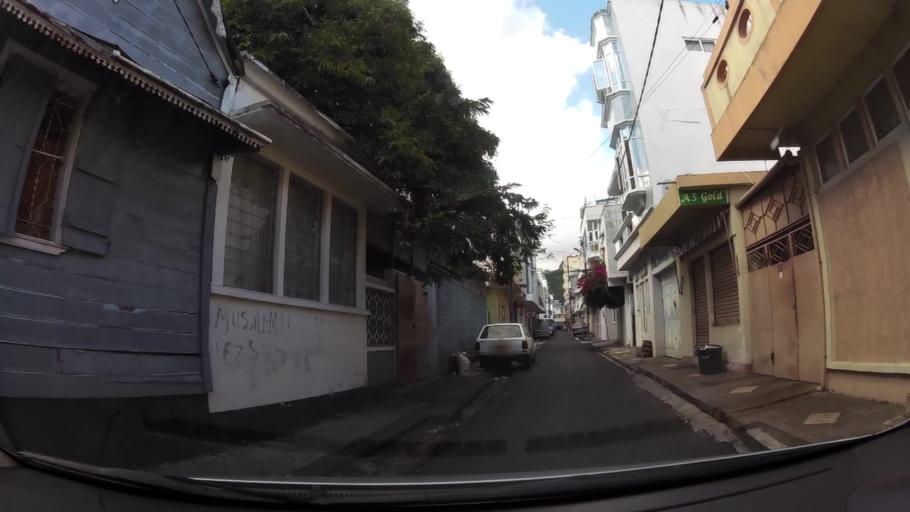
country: MU
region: Port Louis
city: Port Louis
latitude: -20.1610
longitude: 57.5149
